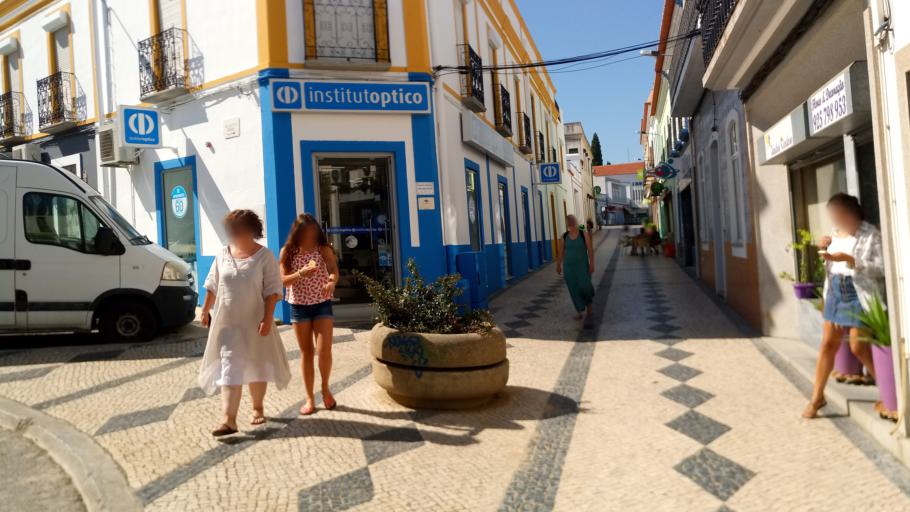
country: PT
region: Evora
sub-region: Reguengos de Monsaraz
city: Reguengos de Monsaraz
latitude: 38.4251
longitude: -7.5340
